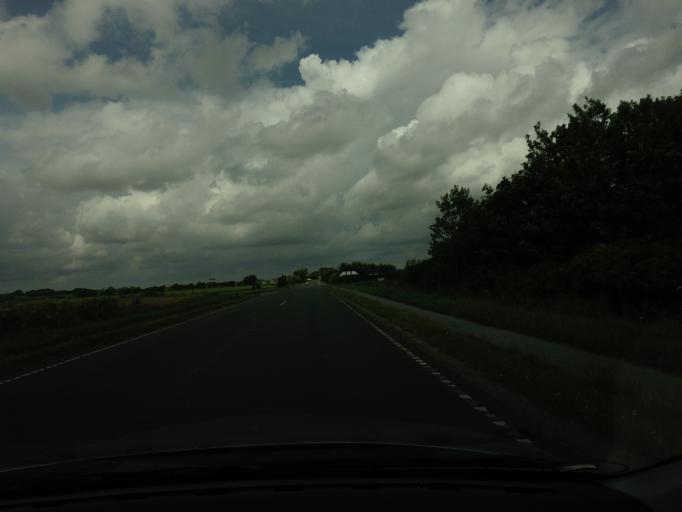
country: DK
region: North Denmark
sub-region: Hjorring Kommune
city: Tars
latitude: 57.3960
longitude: 10.0907
